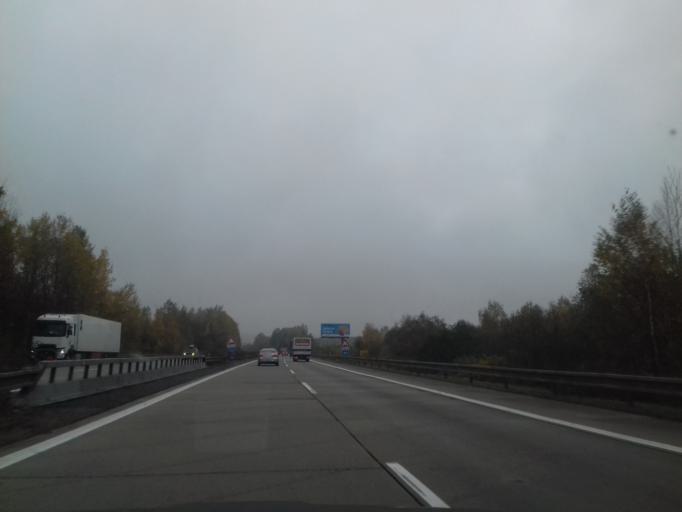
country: CZ
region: Vysocina
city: Heralec
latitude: 49.5003
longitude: 15.4762
